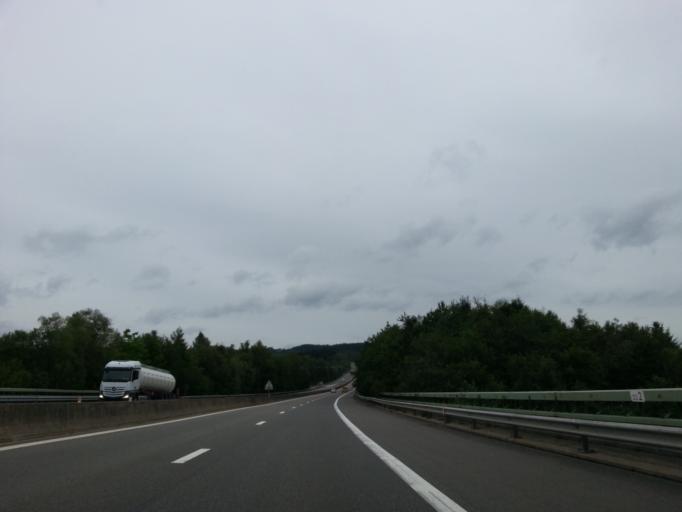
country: BE
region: Wallonia
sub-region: Province de Liege
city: Malmedy
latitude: 50.4153
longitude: 5.9924
